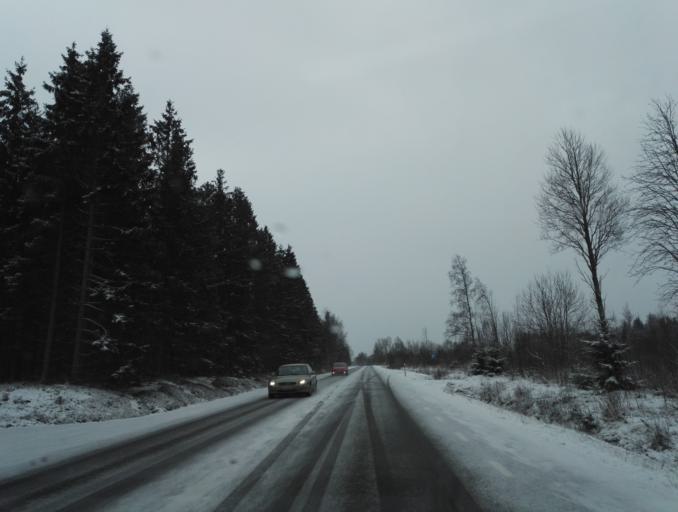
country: SE
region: Kronoberg
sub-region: Uppvidinge Kommun
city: Lenhovda
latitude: 57.0531
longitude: 15.1968
